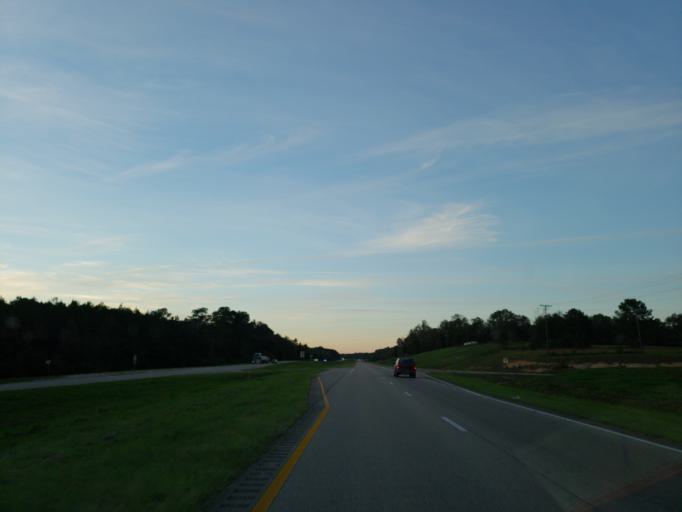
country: US
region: Mississippi
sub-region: Wayne County
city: Belmont
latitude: 31.5891
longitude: -88.5481
